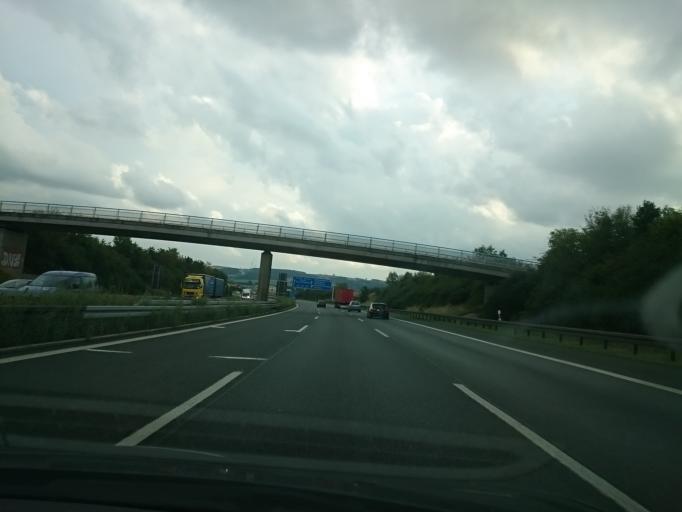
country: DE
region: Bavaria
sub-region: Upper Franconia
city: Himmelkron
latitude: 50.0642
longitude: 11.6195
